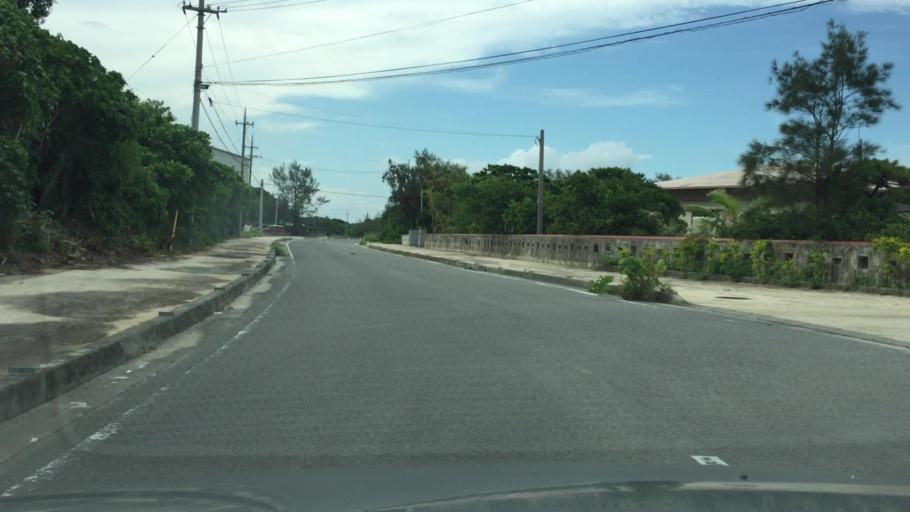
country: JP
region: Okinawa
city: Ishigaki
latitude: 24.4630
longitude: 124.1428
